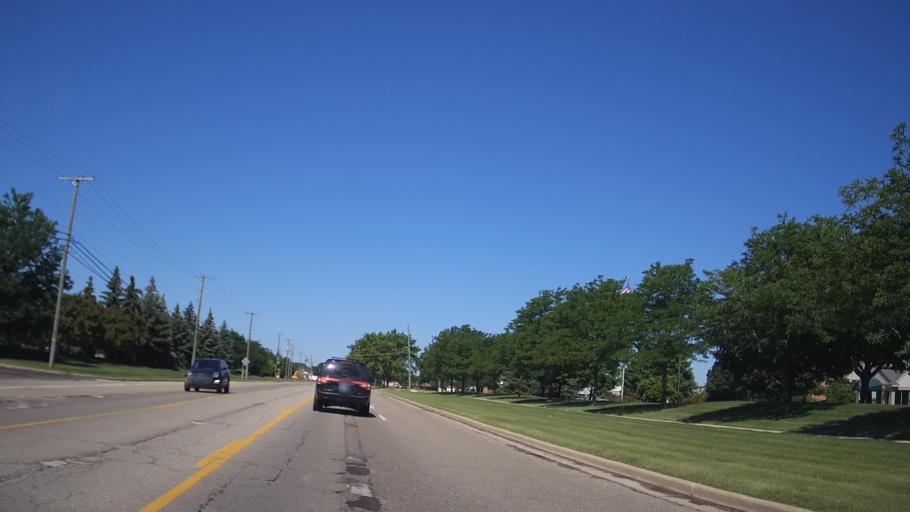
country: US
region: Michigan
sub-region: Macomb County
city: Sterling Heights
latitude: 42.5933
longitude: -83.0832
